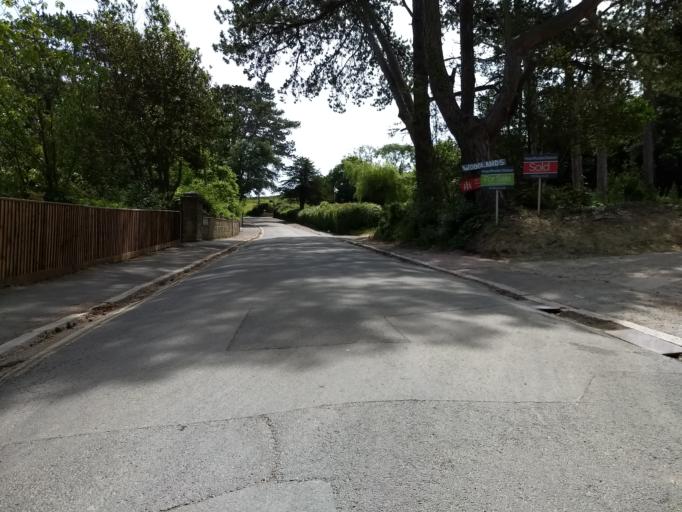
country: GB
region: England
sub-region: Isle of Wight
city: Shanklin
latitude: 50.6216
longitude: -1.1773
